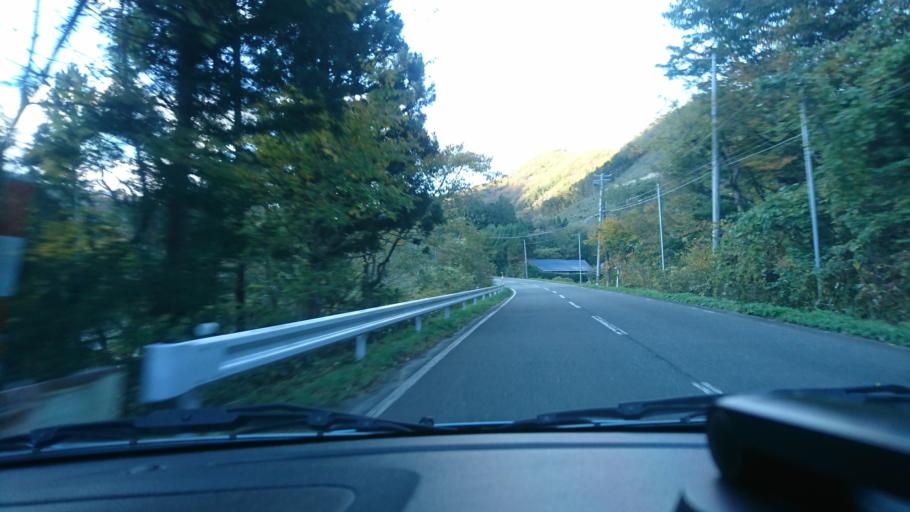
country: JP
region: Miyagi
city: Furukawa
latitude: 38.8351
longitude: 140.7864
